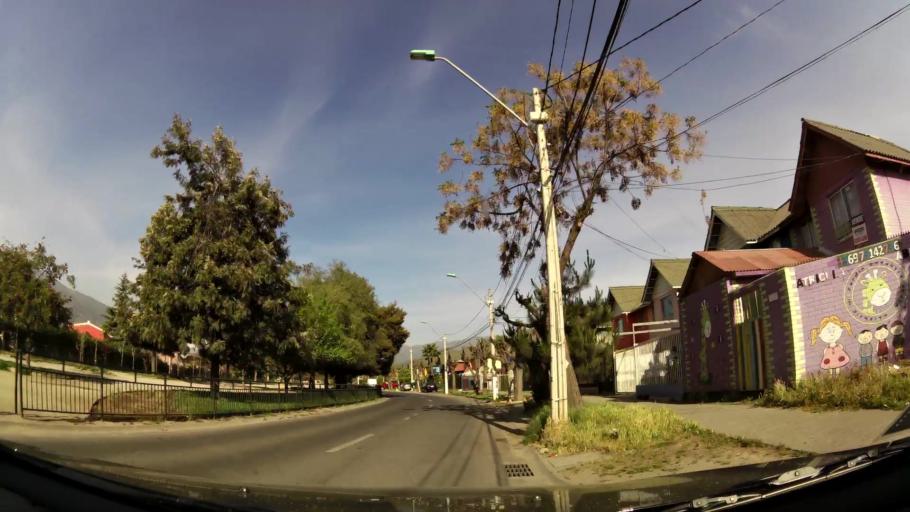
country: CL
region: Santiago Metropolitan
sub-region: Provincia de Cordillera
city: Puente Alto
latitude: -33.5869
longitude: -70.5623
